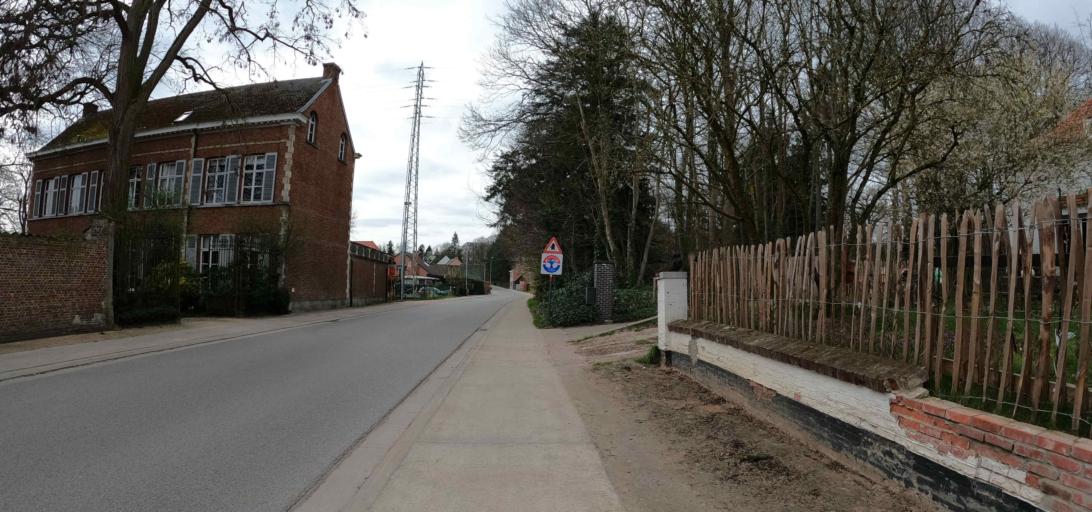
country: BE
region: Flanders
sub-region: Provincie Oost-Vlaanderen
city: Hamme
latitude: 51.1143
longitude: 4.1216
